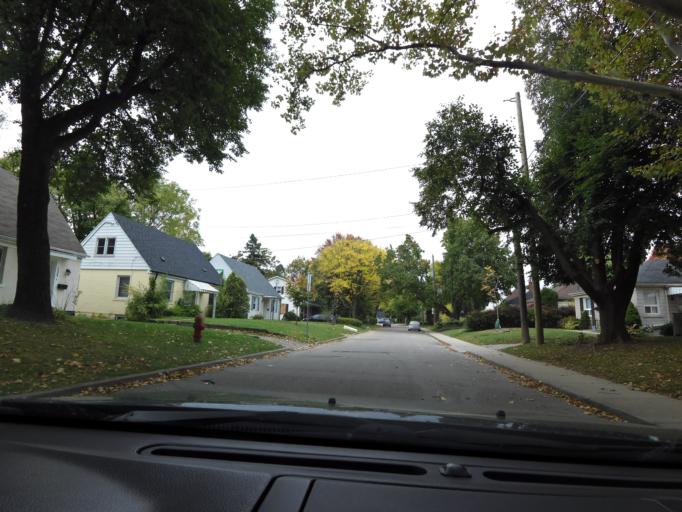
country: CA
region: Ontario
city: Hamilton
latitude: 43.2559
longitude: -79.9147
